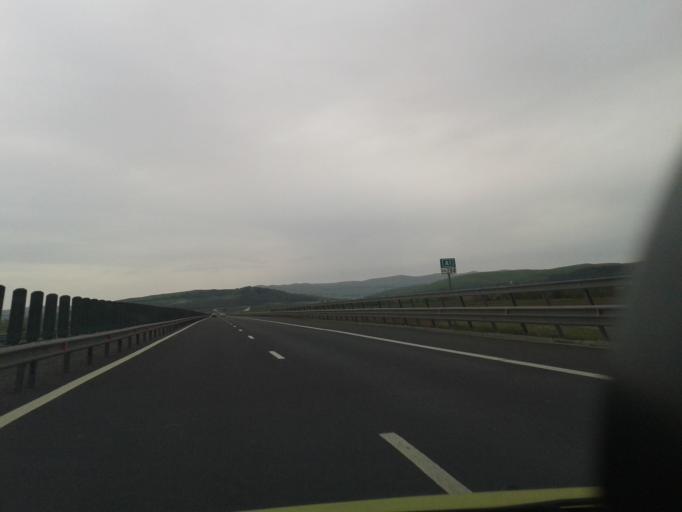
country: RO
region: Sibiu
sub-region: Oras Miercurea Sibiului
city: Miercurea Sibiului
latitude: 45.8936
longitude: 23.8190
